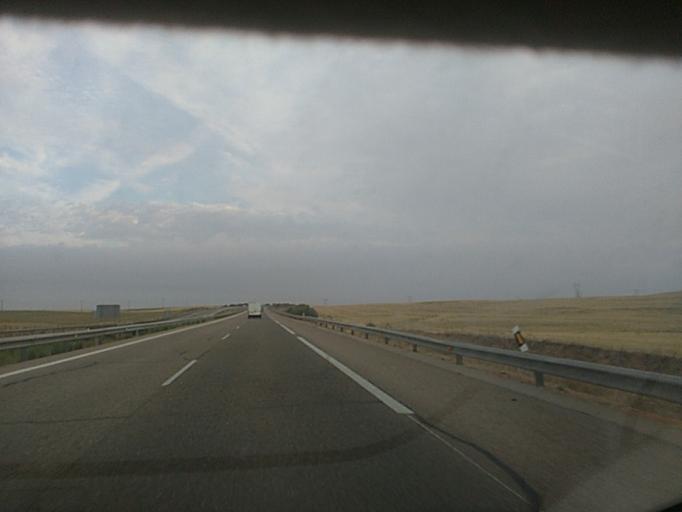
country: ES
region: Castille and Leon
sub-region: Provincia de Zamora
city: Cerecinos de Campos
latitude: 41.9094
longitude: -5.5003
